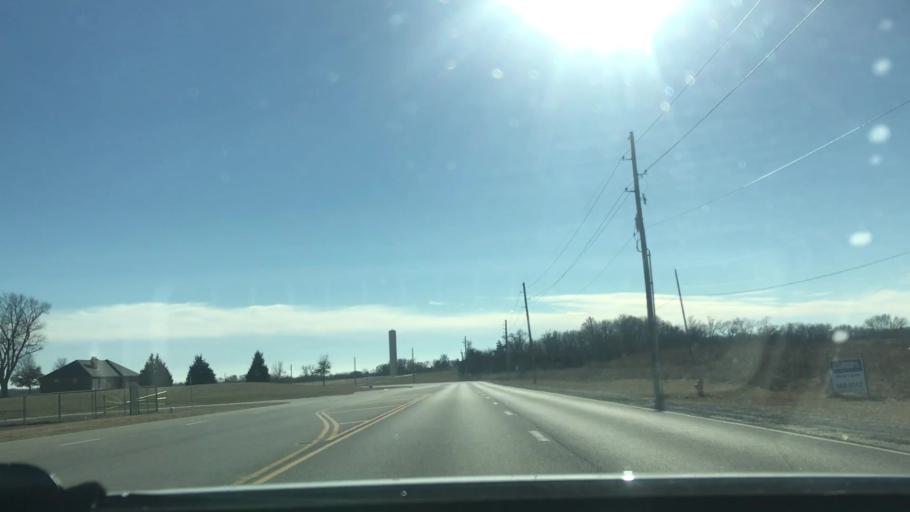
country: US
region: Kansas
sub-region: Wyandotte County
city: Bonner Springs
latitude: 39.1147
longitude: -94.8538
